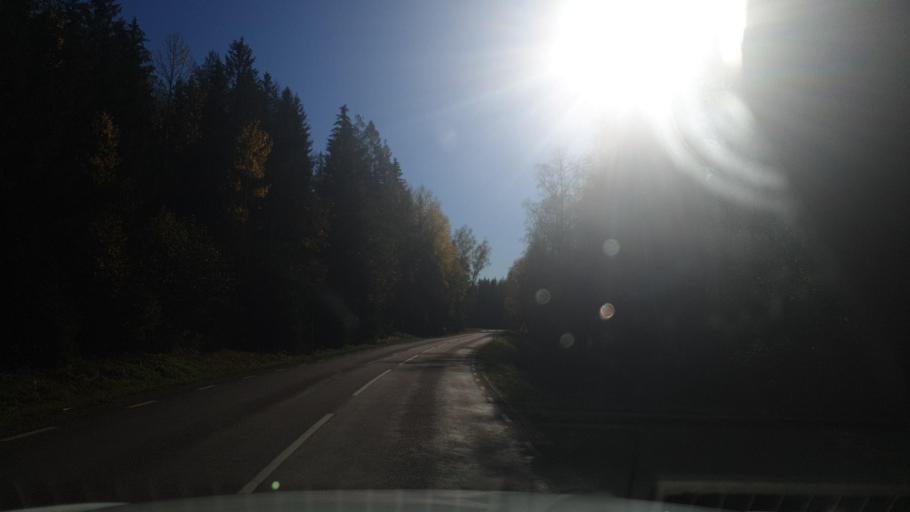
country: SE
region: Vaermland
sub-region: Grums Kommun
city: Slottsbron
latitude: 59.4230
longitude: 12.9812
